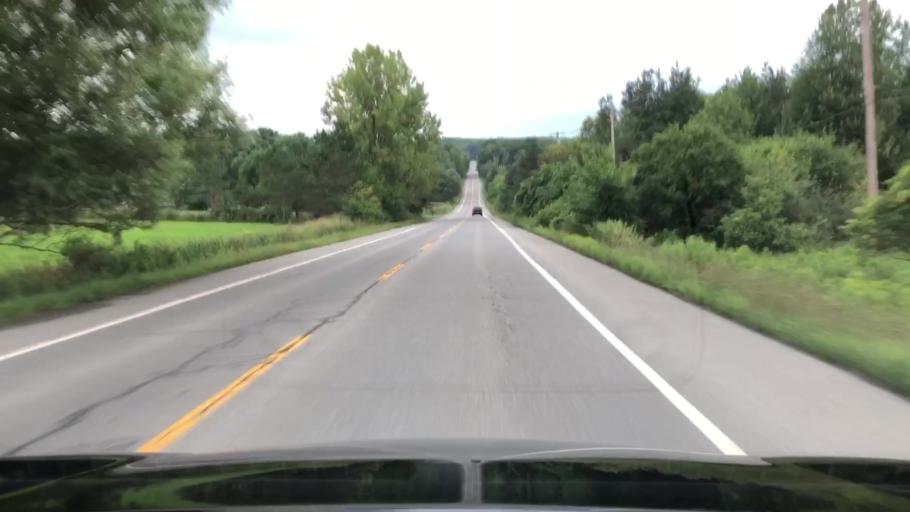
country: US
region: New York
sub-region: Erie County
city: Orchard Park
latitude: 42.7646
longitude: -78.6969
